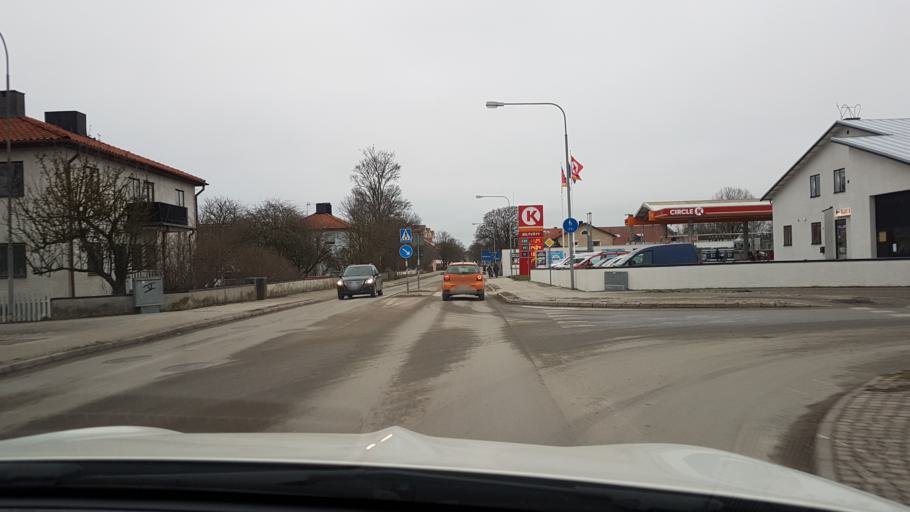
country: SE
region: Gotland
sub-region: Gotland
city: Visby
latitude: 57.6296
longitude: 18.2861
